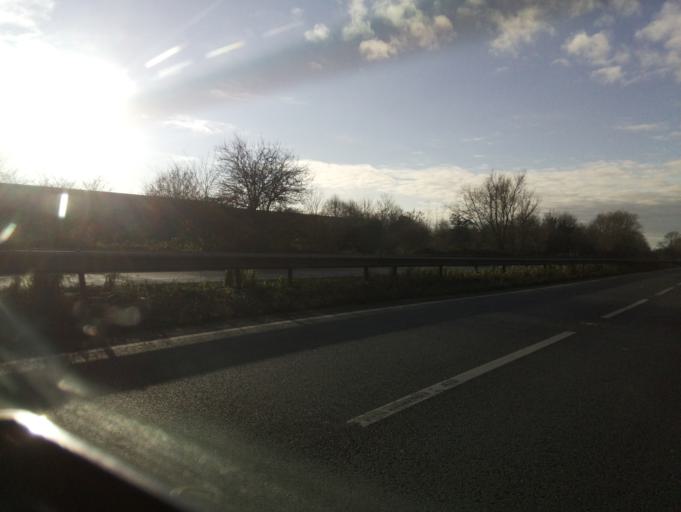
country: GB
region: England
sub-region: Staffordshire
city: Burton upon Trent
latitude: 52.8237
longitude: -1.6351
